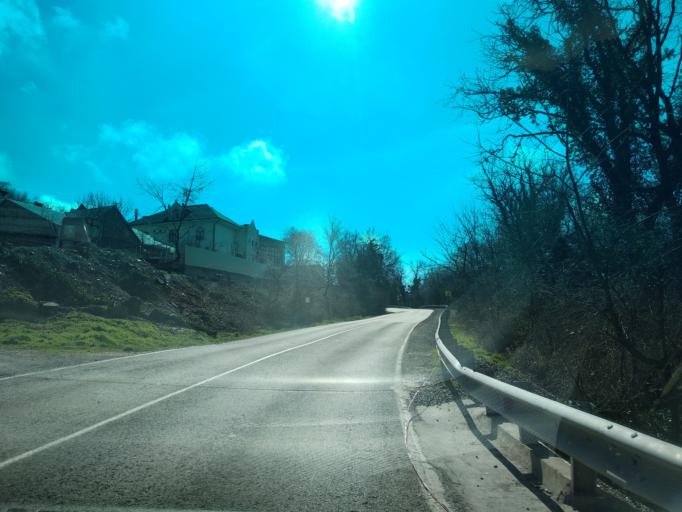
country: RU
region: Krasnodarskiy
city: Tuapse
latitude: 44.0896
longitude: 39.1229
